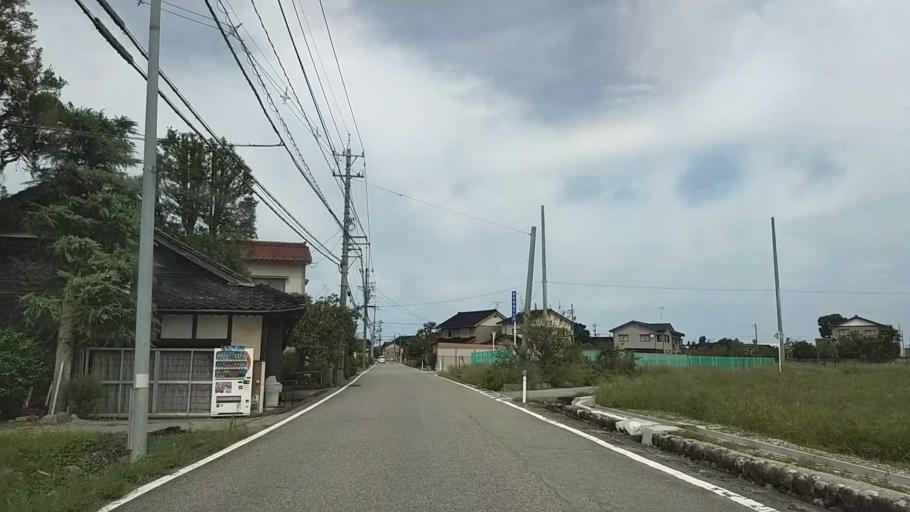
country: JP
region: Toyama
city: Kamiichi
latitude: 36.7384
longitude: 137.3736
